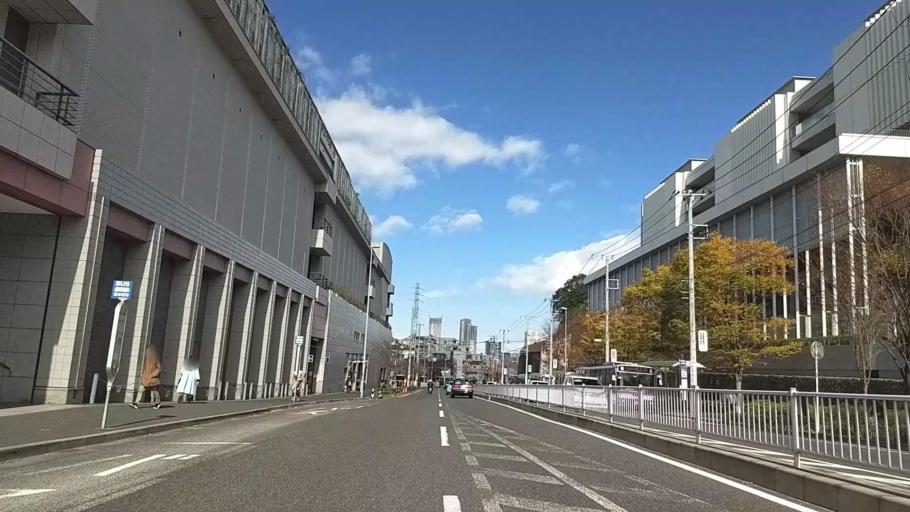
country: JP
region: Kanagawa
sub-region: Kawasaki-shi
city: Kawasaki
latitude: 35.5539
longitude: 139.6474
